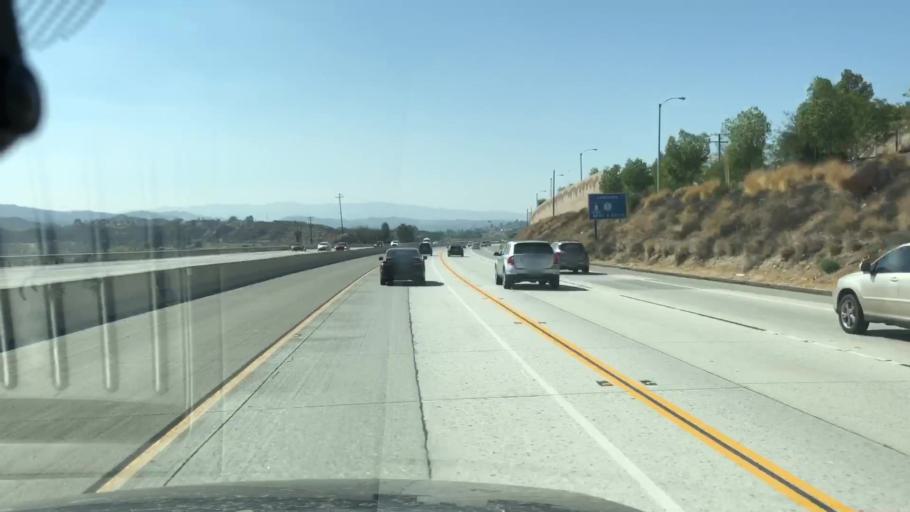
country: US
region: California
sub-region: Los Angeles County
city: Agua Dulce
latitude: 34.4296
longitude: -118.4023
